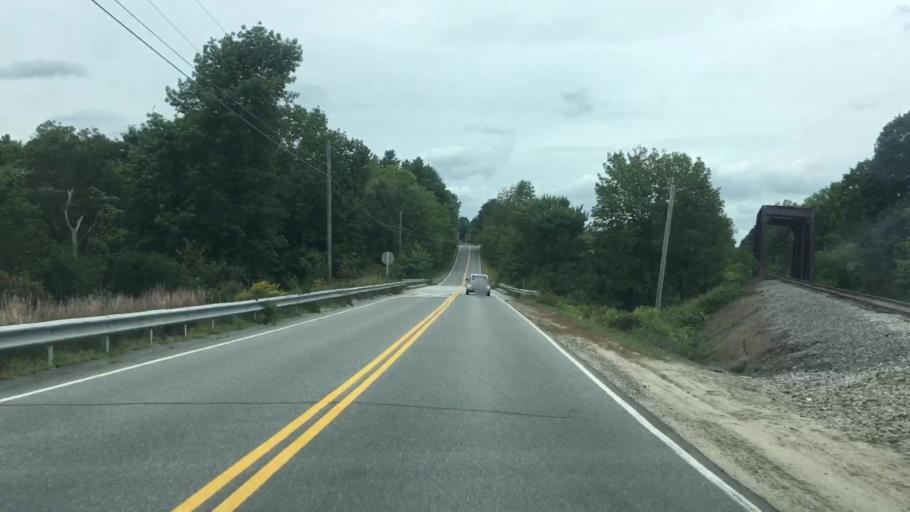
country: US
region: Maine
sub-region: Cumberland County
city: Yarmouth
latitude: 43.8603
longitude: -70.2195
